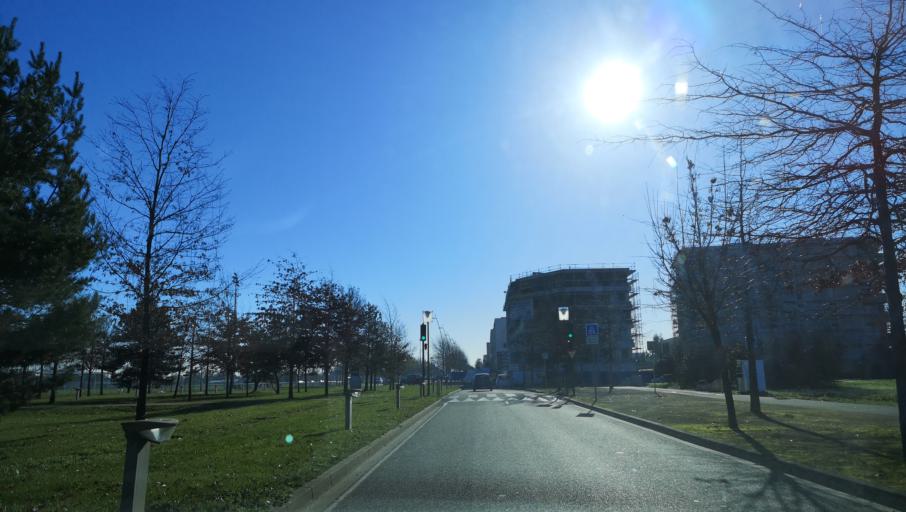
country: FR
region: Midi-Pyrenees
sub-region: Departement de la Haute-Garonne
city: Beauzelle
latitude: 43.6555
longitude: 1.3777
